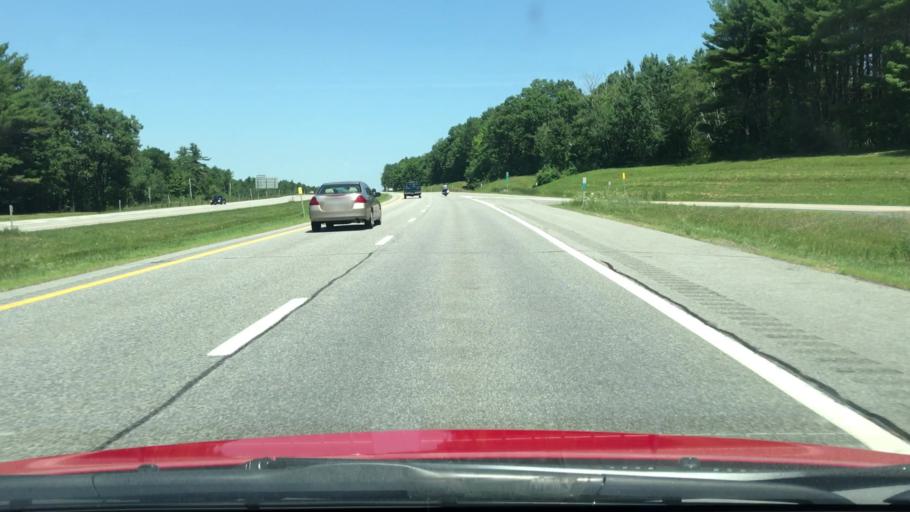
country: US
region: New York
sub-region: Essex County
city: Keeseville
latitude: 44.4464
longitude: -73.4900
